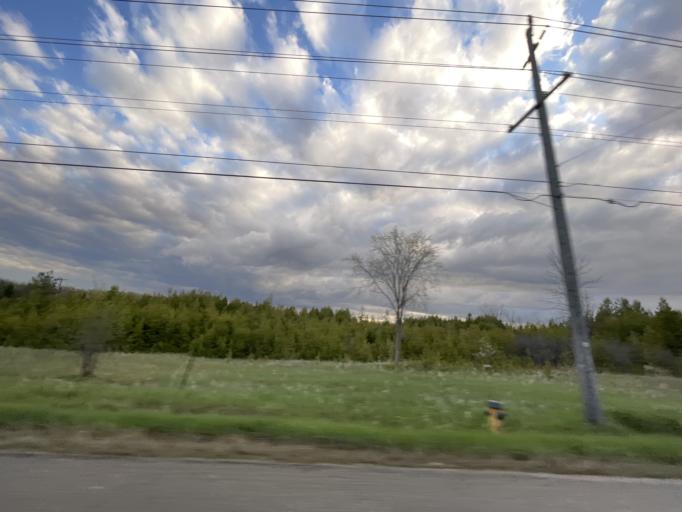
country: CA
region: Ontario
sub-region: Wellington County
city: Guelph
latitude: 43.5912
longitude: -80.2786
